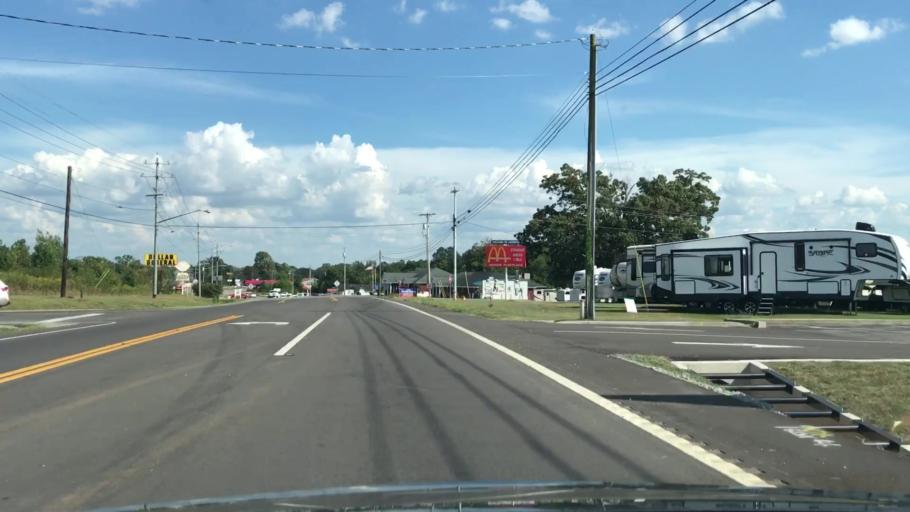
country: US
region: Alabama
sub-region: Limestone County
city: Ardmore
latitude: 34.9967
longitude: -86.8598
